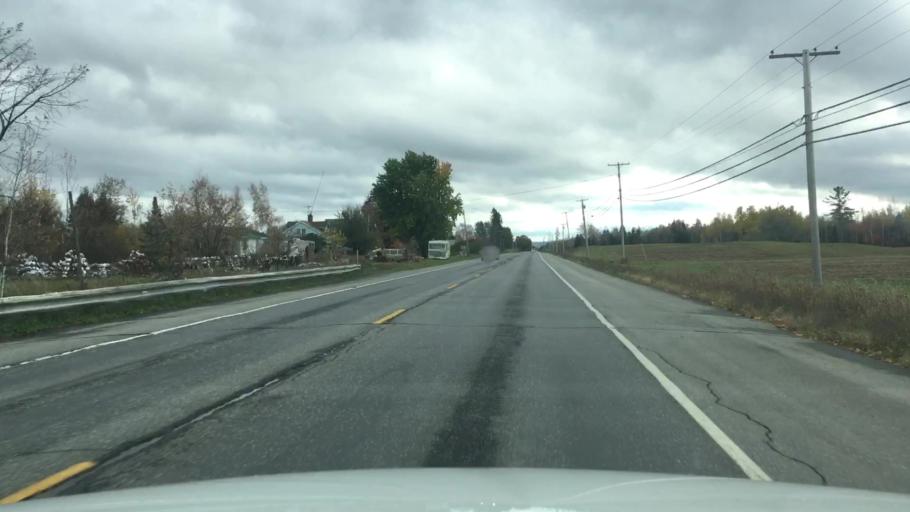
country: US
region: Maine
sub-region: Aroostook County
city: Houlton
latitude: 46.1889
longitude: -67.8413
